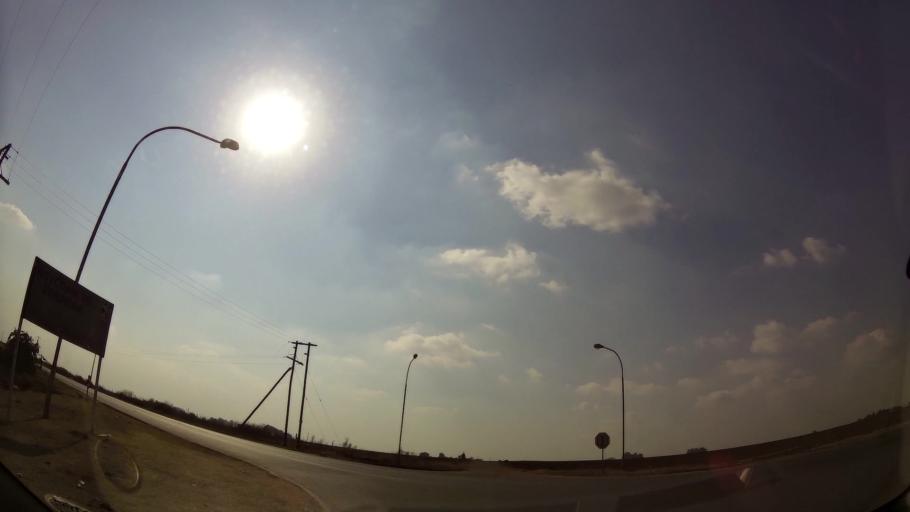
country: ZA
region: Gauteng
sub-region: Ekurhuleni Metropolitan Municipality
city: Springs
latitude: -26.1263
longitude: 28.4902
